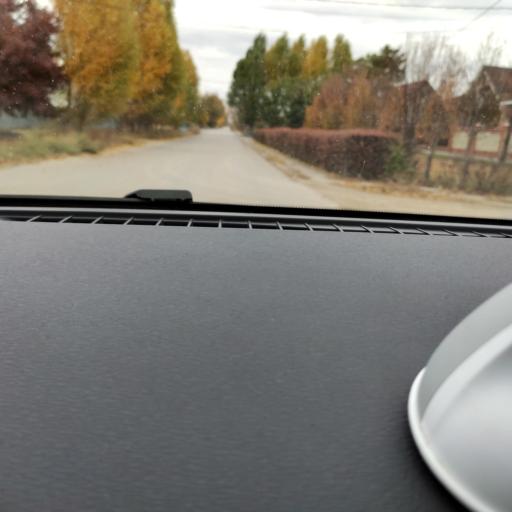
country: RU
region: Samara
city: Smyshlyayevka
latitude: 53.2393
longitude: 50.3207
